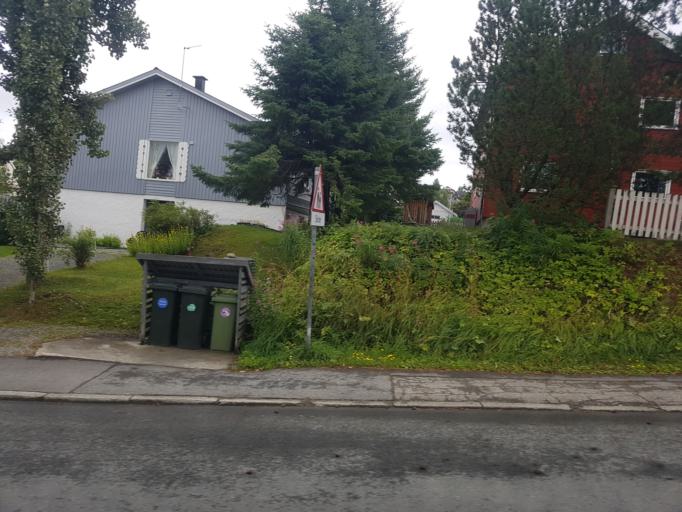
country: NO
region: Sor-Trondelag
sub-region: Trondheim
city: Trondheim
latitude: 63.3990
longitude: 10.4092
